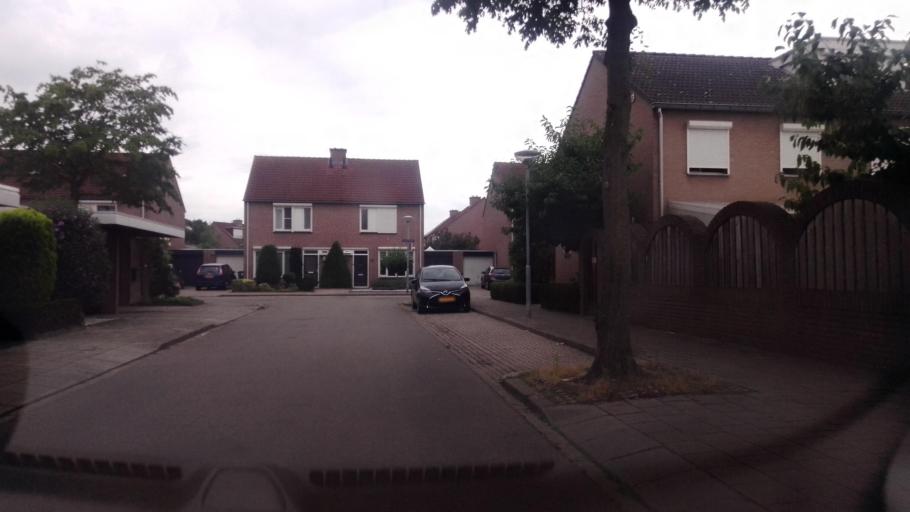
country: NL
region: Limburg
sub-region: Gemeente Venlo
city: Tegelen
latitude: 51.3795
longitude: 6.1264
